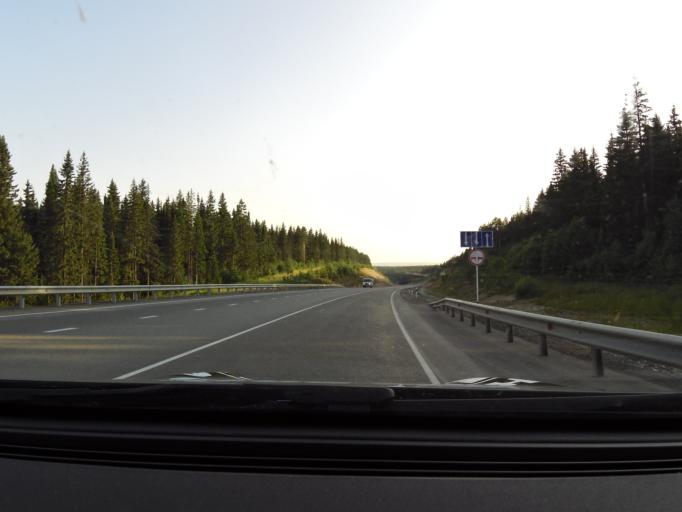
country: RU
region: Sverdlovsk
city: Nizhniye Sergi
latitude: 56.6573
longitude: 59.2650
